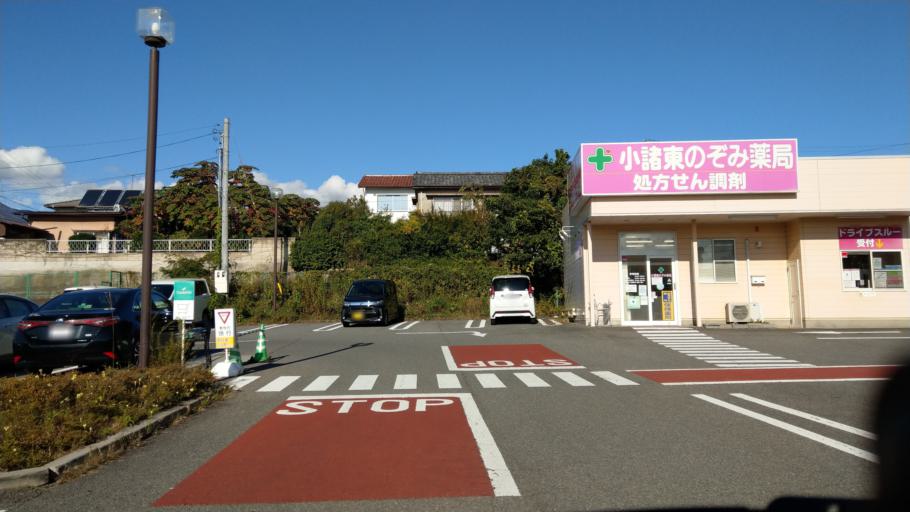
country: JP
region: Nagano
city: Komoro
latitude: 36.3167
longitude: 138.4368
